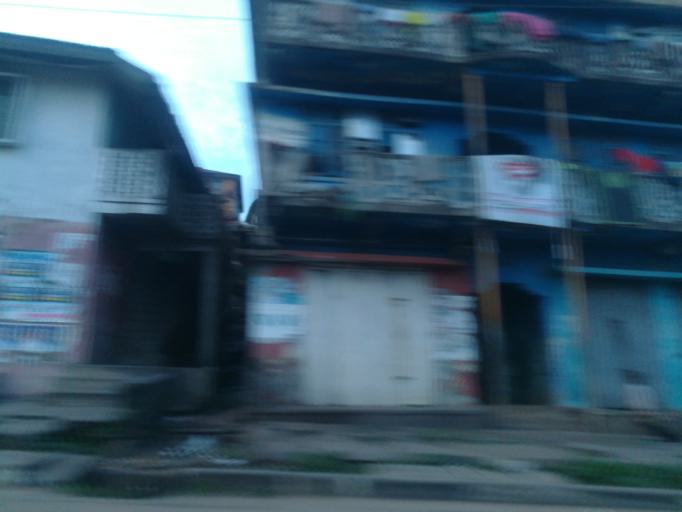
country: NG
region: Oyo
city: Ibadan
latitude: 7.3848
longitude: 3.8995
